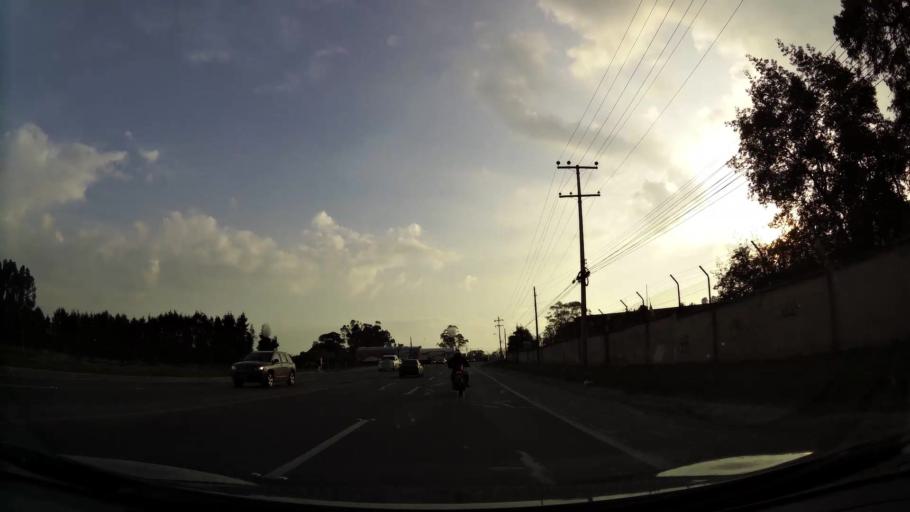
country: CO
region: Cundinamarca
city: Cota
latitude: 4.7897
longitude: -74.1187
